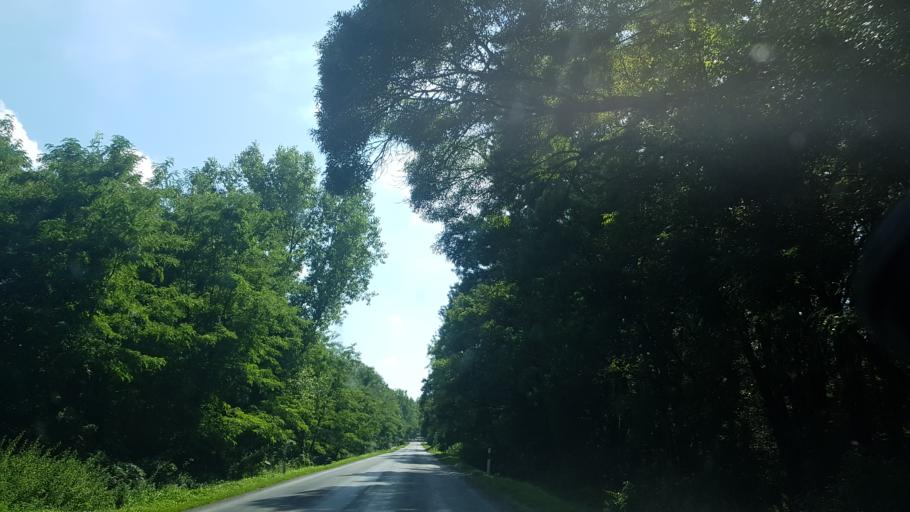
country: HU
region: Somogy
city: Segesd
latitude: 46.3718
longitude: 17.3600
